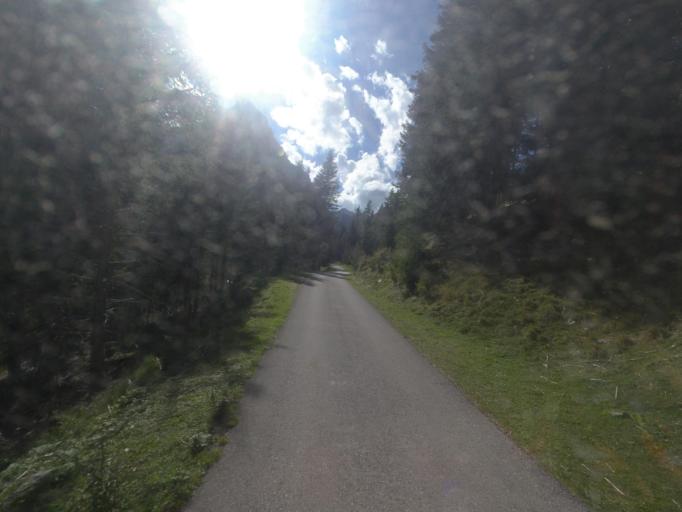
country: AT
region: Salzburg
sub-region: Politischer Bezirk Tamsweg
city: Zederhaus
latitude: 47.1850
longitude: 13.3931
